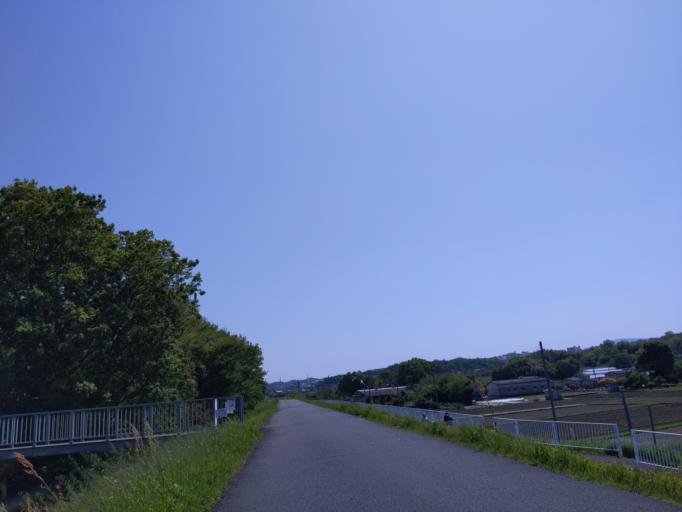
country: JP
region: Nara
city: Nara-shi
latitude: 34.7530
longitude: 135.8002
